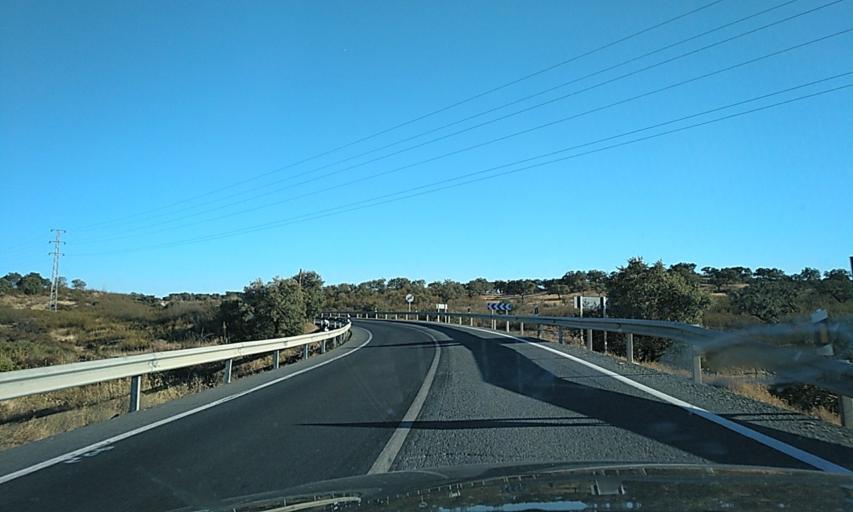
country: ES
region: Andalusia
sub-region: Provincia de Huelva
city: San Bartolome de la Torre
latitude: 37.4729
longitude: -7.1264
